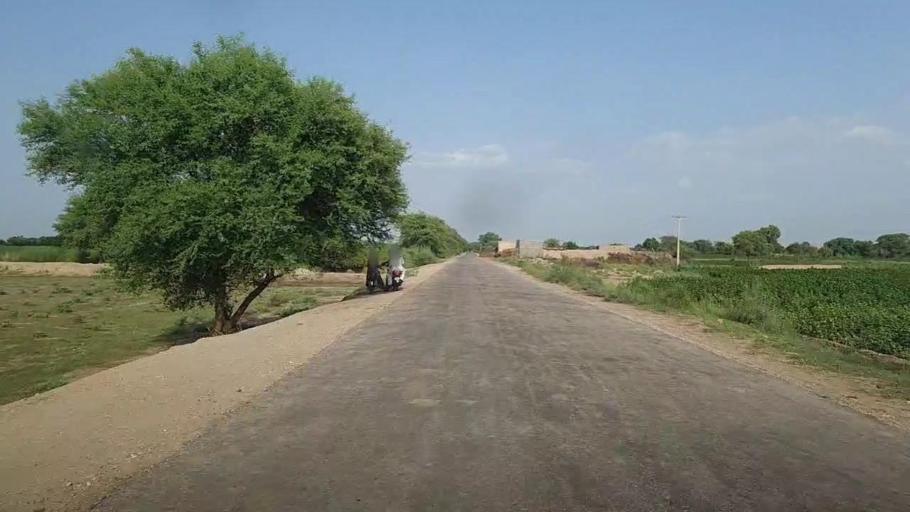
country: PK
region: Sindh
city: Khairpur
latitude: 28.0760
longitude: 69.8057
